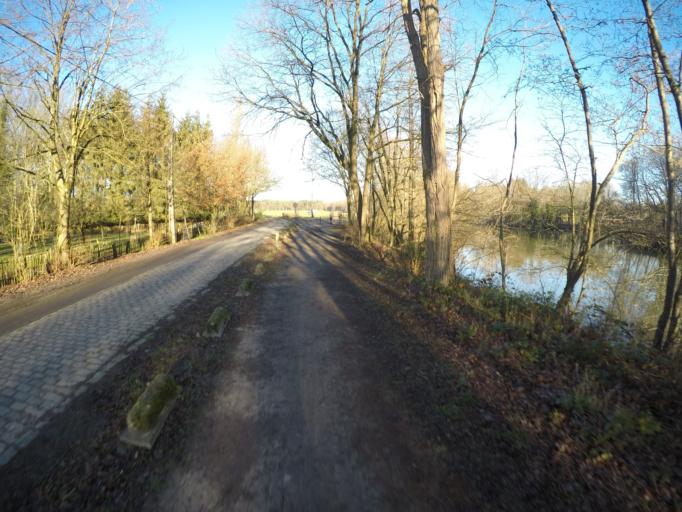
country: BE
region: Flanders
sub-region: Provincie Antwerpen
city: Schilde
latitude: 51.2255
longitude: 4.6124
